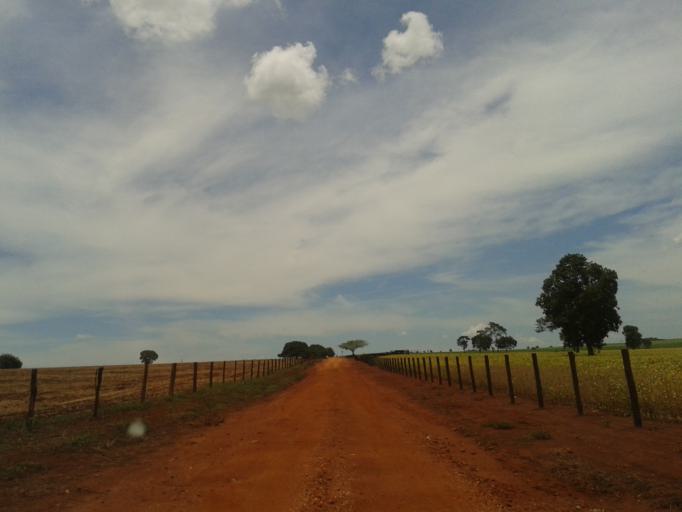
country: BR
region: Minas Gerais
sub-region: Capinopolis
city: Capinopolis
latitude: -18.7052
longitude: -49.7127
